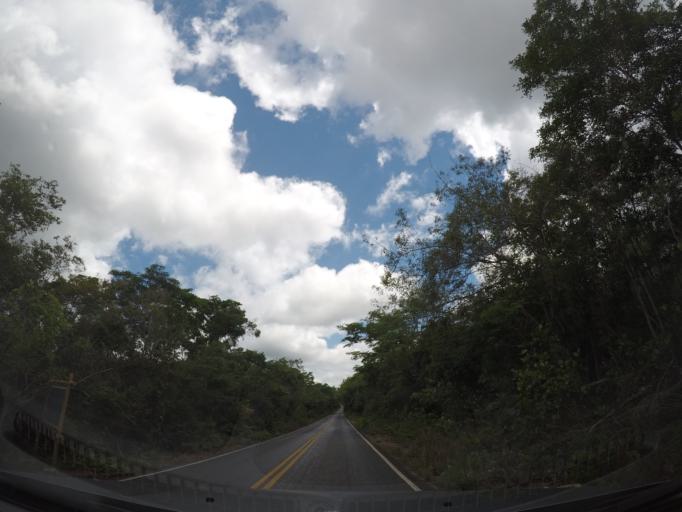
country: BR
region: Bahia
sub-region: Andarai
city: Vera Cruz
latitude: -12.5333
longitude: -41.3656
